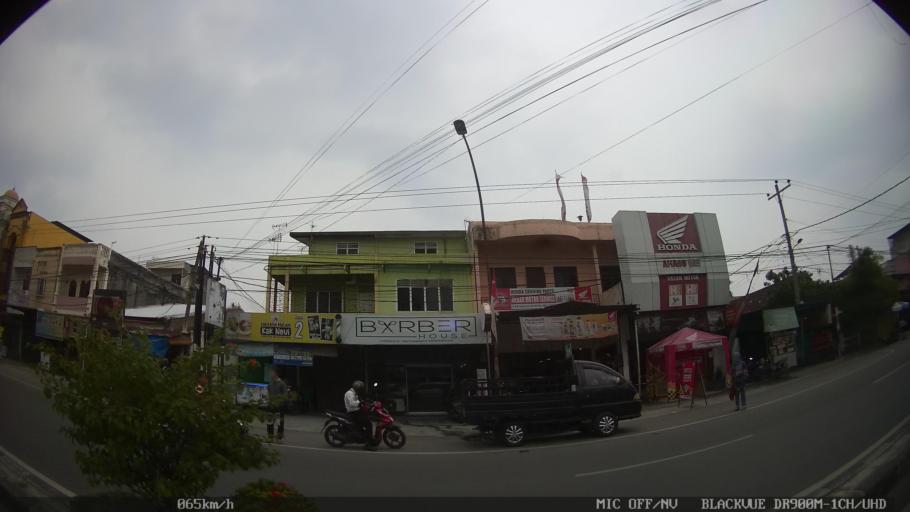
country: ID
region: North Sumatra
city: Medan
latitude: 3.5711
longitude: 98.7032
